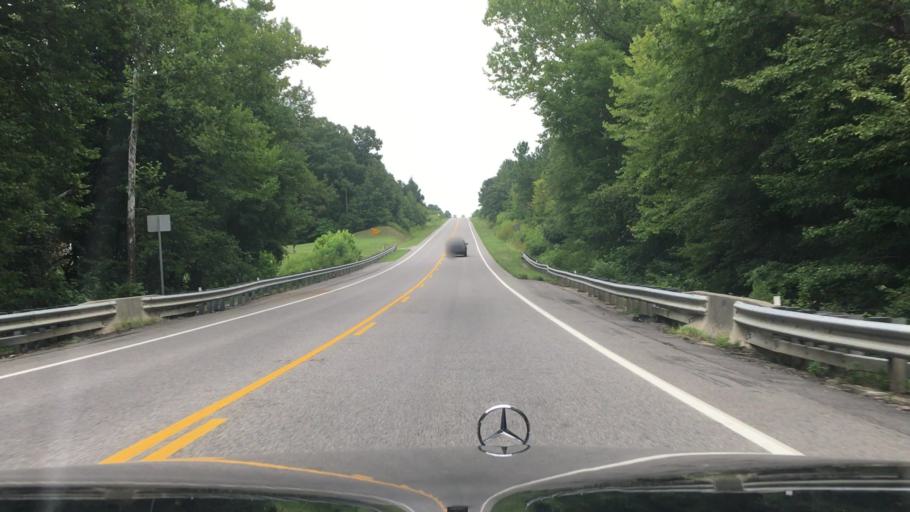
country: US
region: Virginia
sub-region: Nottoway County
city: Crewe
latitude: 37.2769
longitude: -78.2235
